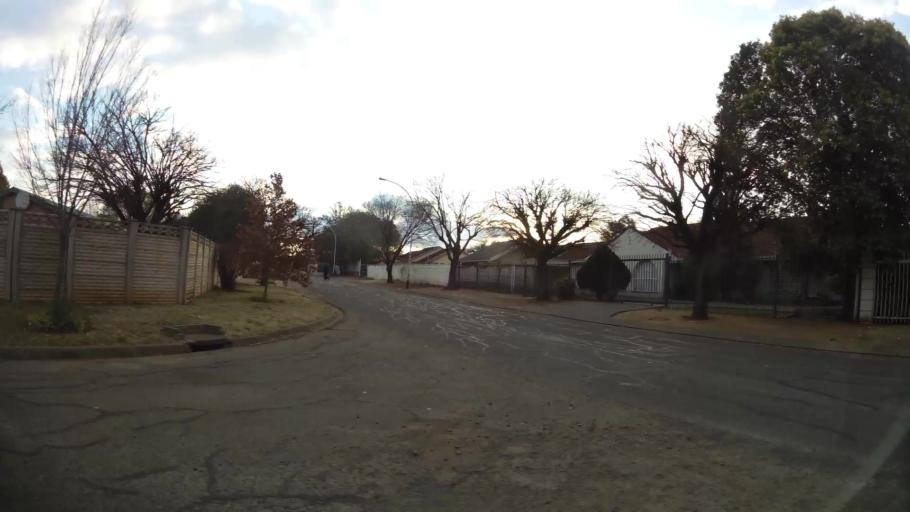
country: ZA
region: Orange Free State
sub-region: Mangaung Metropolitan Municipality
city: Bloemfontein
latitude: -29.1401
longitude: 26.1734
